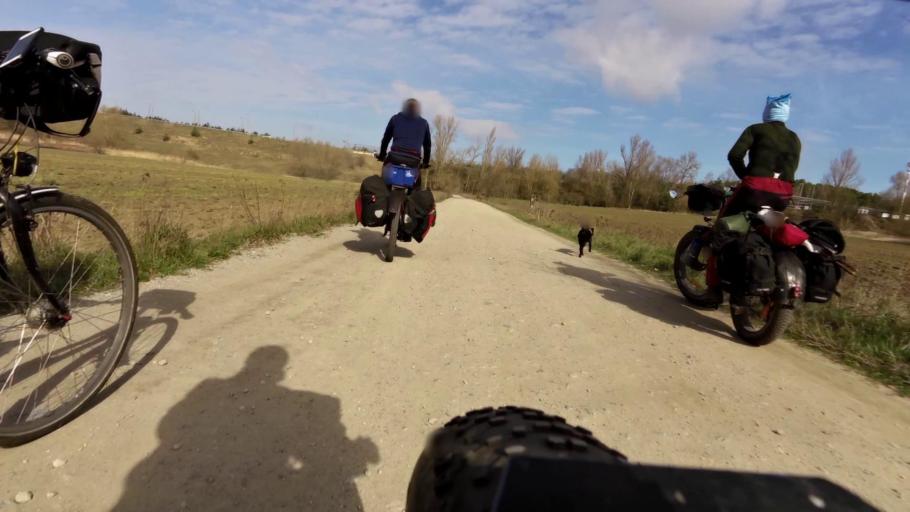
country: PL
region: Lubusz
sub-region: Powiat slubicki
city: Slubice
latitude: 52.3143
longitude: 14.5872
